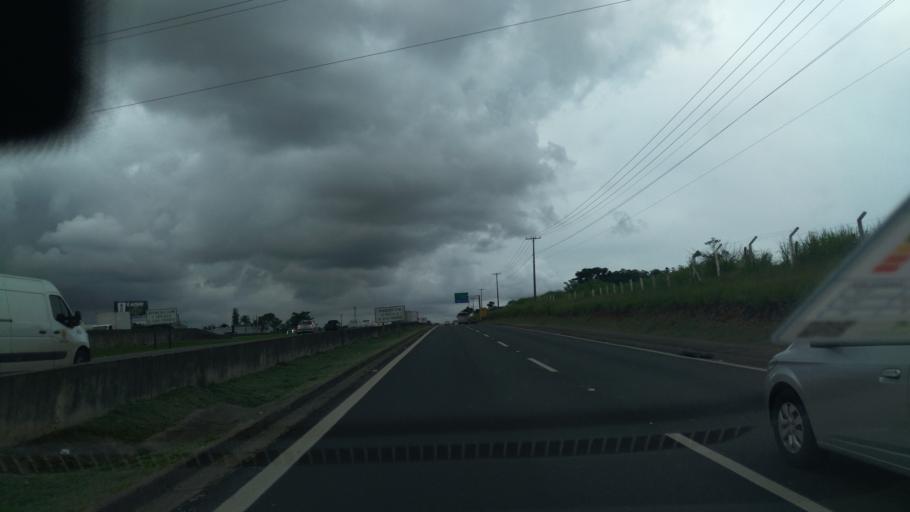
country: BR
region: Sao Paulo
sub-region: Campinas
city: Campinas
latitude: -22.8774
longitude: -47.1205
